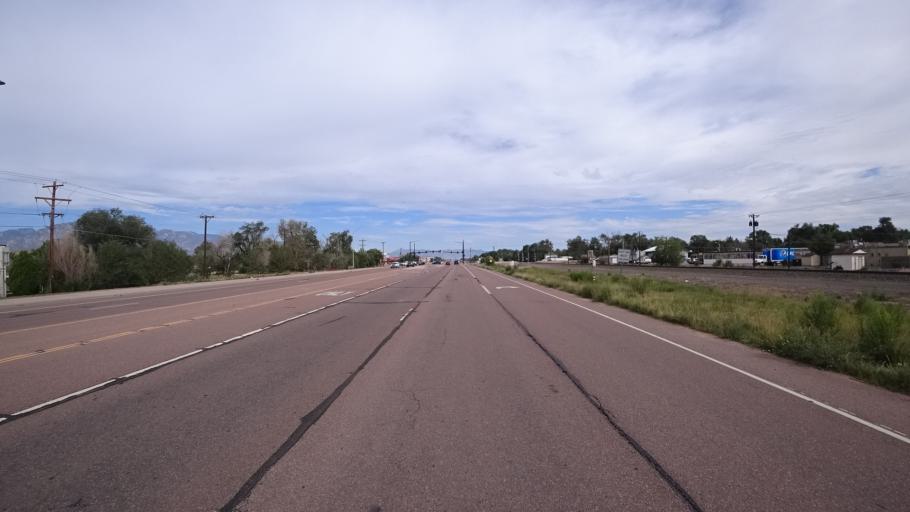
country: US
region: Colorado
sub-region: El Paso County
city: Security-Widefield
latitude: 38.7354
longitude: -104.7294
